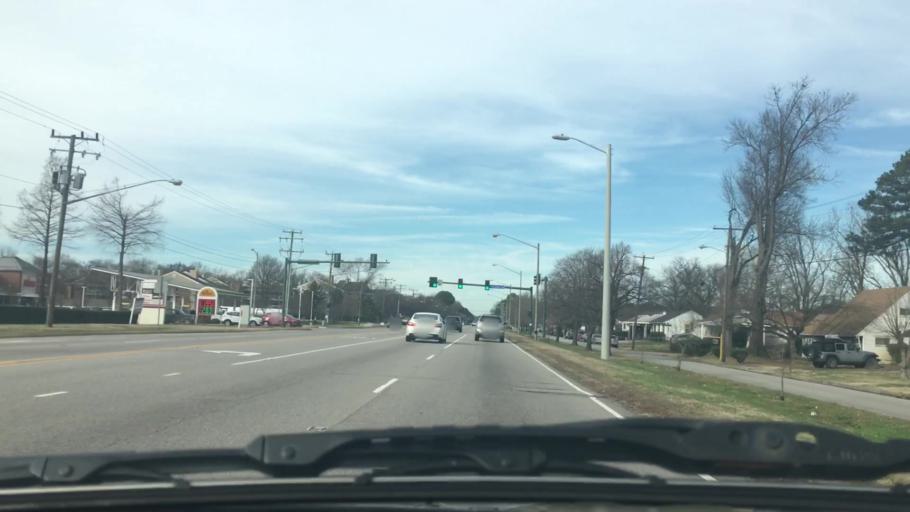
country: US
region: Virginia
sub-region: City of Norfolk
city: Norfolk
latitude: 36.8964
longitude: -76.2246
